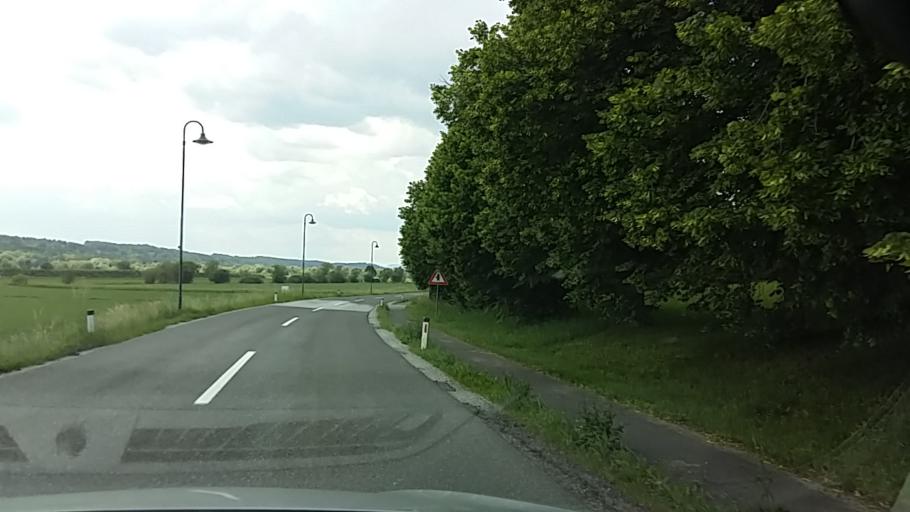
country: AT
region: Styria
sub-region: Politischer Bezirk Hartberg-Fuerstenfeld
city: Hainersdorf
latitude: 47.0994
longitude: 15.9693
